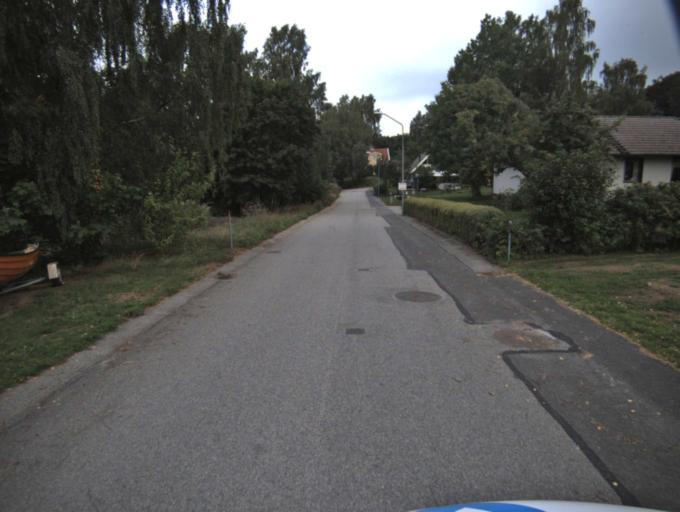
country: SE
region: Vaestra Goetaland
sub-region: Ulricehamns Kommun
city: Ulricehamn
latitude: 57.7431
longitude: 13.4199
